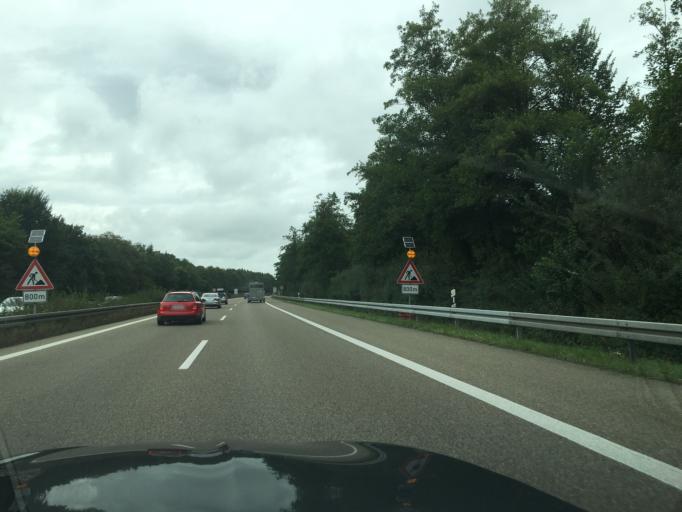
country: DE
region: Bavaria
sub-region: Swabia
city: Holzheim
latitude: 48.3587
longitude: 10.0816
